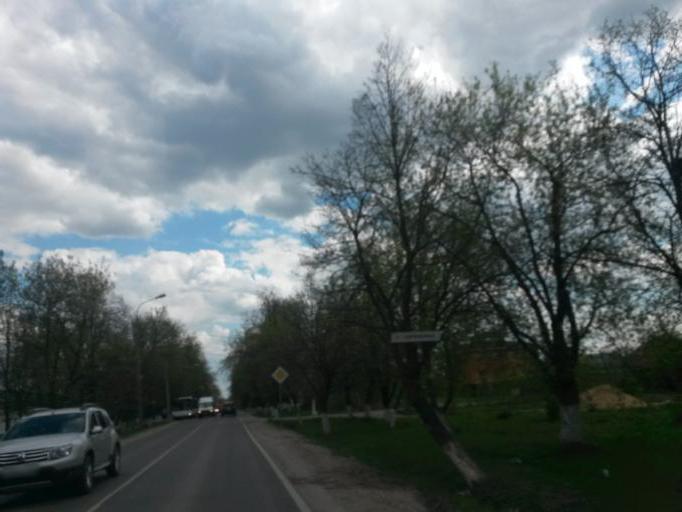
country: RU
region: Moskovskaya
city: Klimovsk
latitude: 55.3520
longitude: 37.5412
